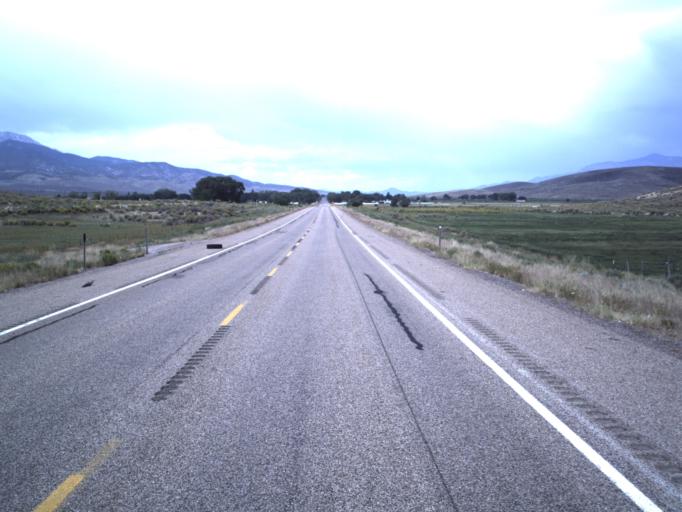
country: US
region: Utah
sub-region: Piute County
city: Junction
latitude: 38.2188
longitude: -112.2197
